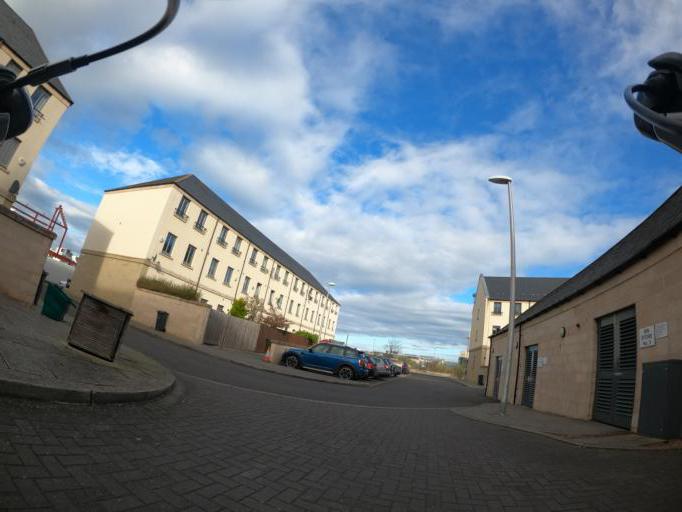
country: GB
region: Scotland
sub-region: Edinburgh
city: Edinburgh
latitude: 55.9828
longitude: -3.1932
